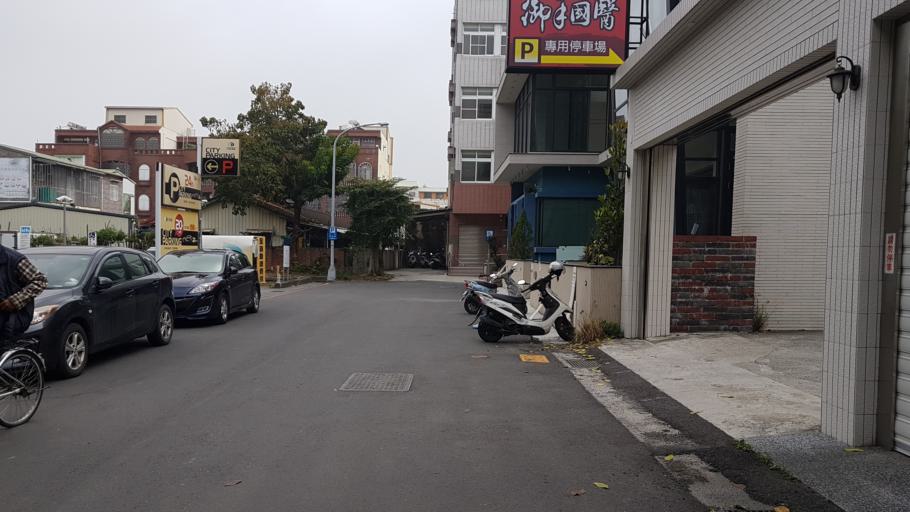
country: TW
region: Taiwan
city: Xinying
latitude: 23.3078
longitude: 120.3169
